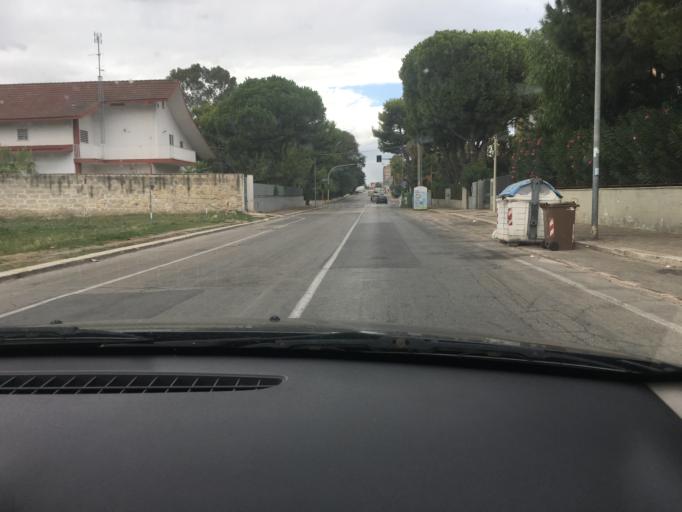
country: IT
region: Apulia
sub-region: Provincia di Bari
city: Bari
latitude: 41.1320
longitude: 16.8331
